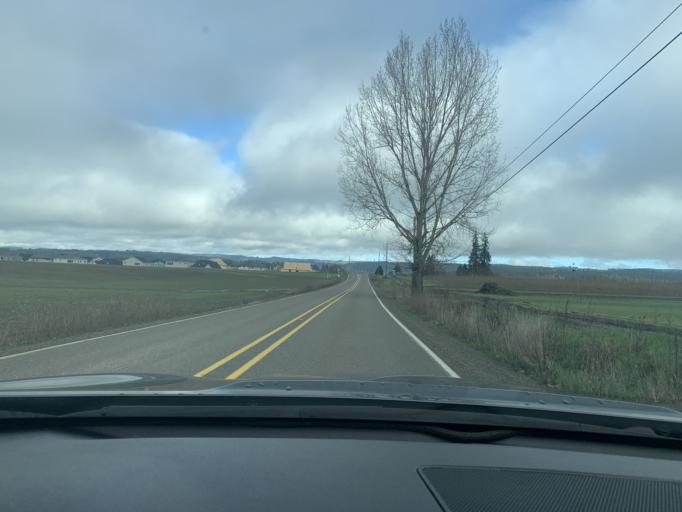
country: US
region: Oregon
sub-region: Washington County
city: North Plains
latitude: 45.5906
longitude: -122.9691
